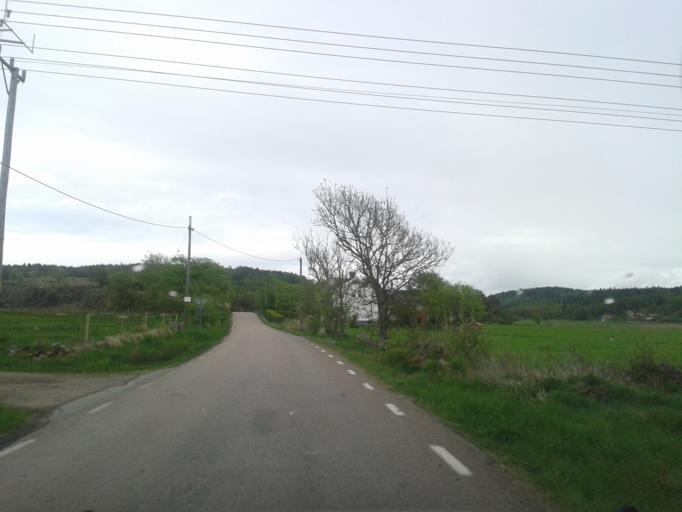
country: SE
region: Vaestra Goetaland
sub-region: Kungalvs Kommun
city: Kode
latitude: 57.9159
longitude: 11.8049
